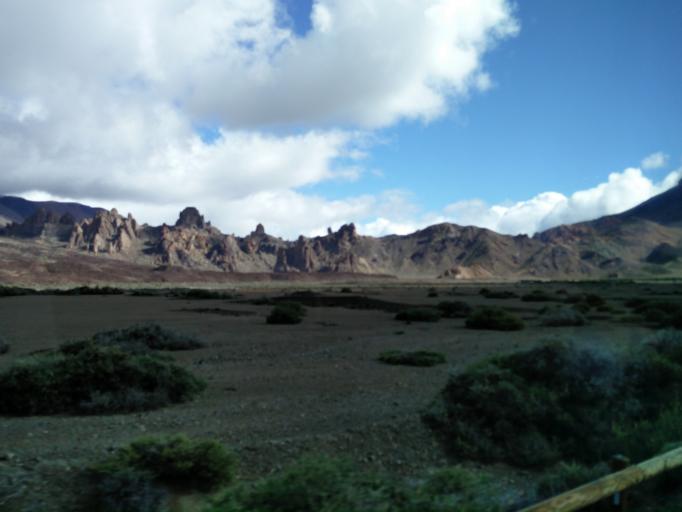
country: ES
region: Canary Islands
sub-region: Provincia de Santa Cruz de Tenerife
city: Vilaflor
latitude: 28.2106
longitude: -16.6501
